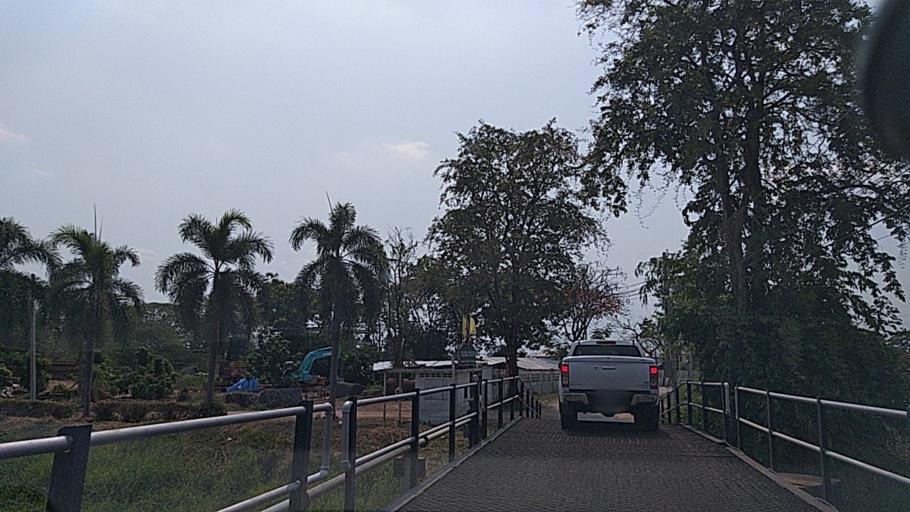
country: TH
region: Sara Buri
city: Nong Khae
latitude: 14.3309
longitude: 100.8743
